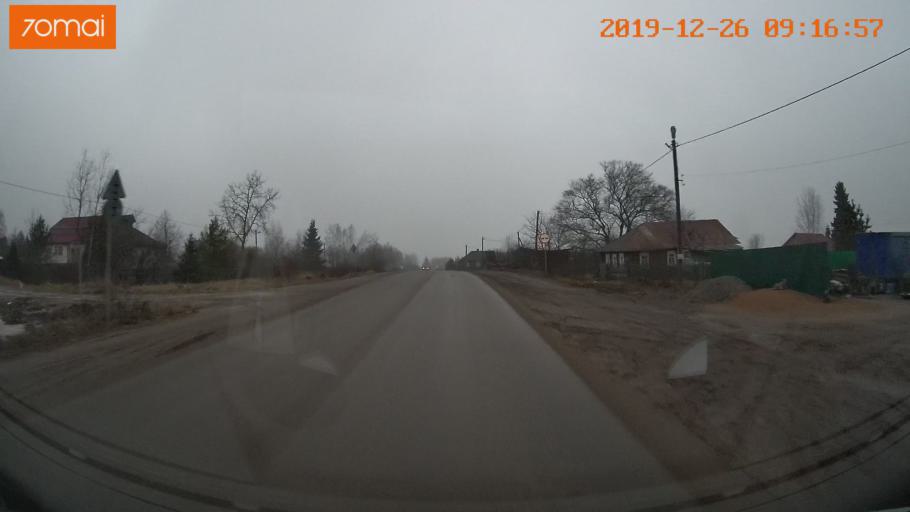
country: RU
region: Vologda
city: Gryazovets
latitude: 58.9245
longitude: 40.2392
